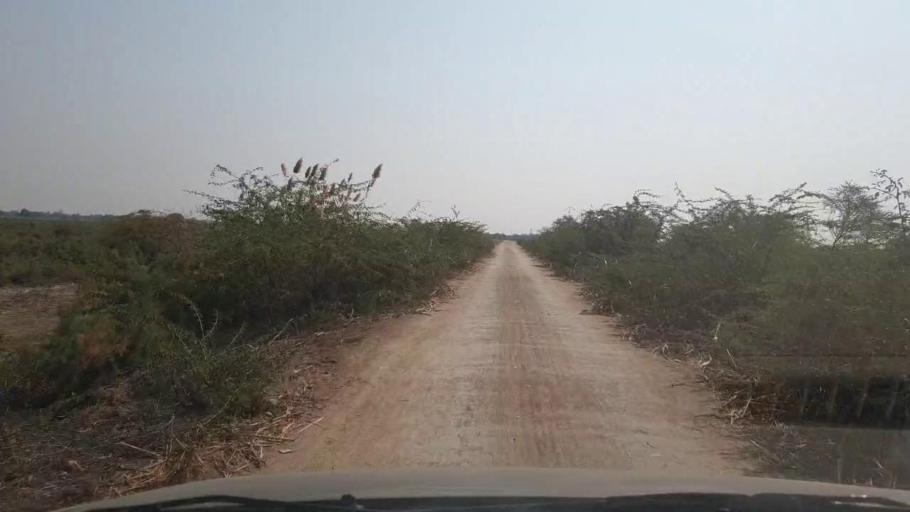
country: PK
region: Sindh
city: Mirwah Gorchani
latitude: 25.2899
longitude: 69.1495
